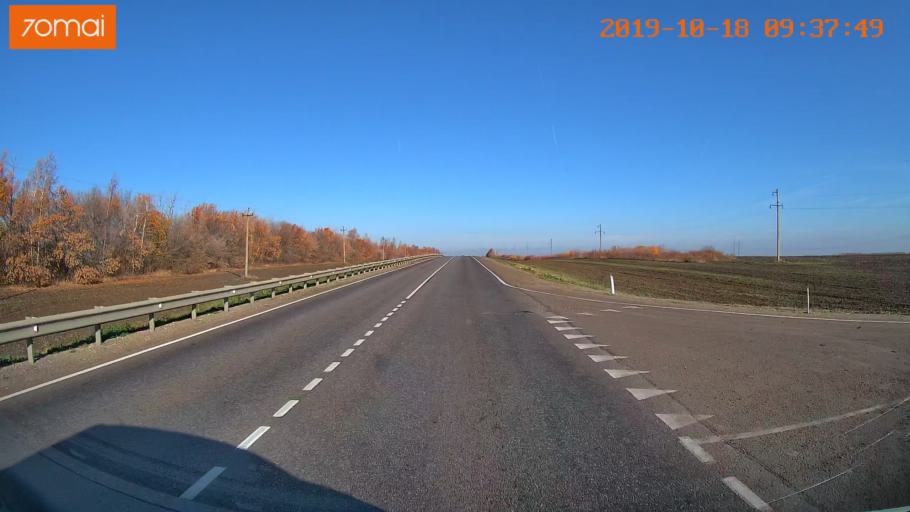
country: RU
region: Tula
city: Yefremov
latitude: 53.2284
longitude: 38.1395
